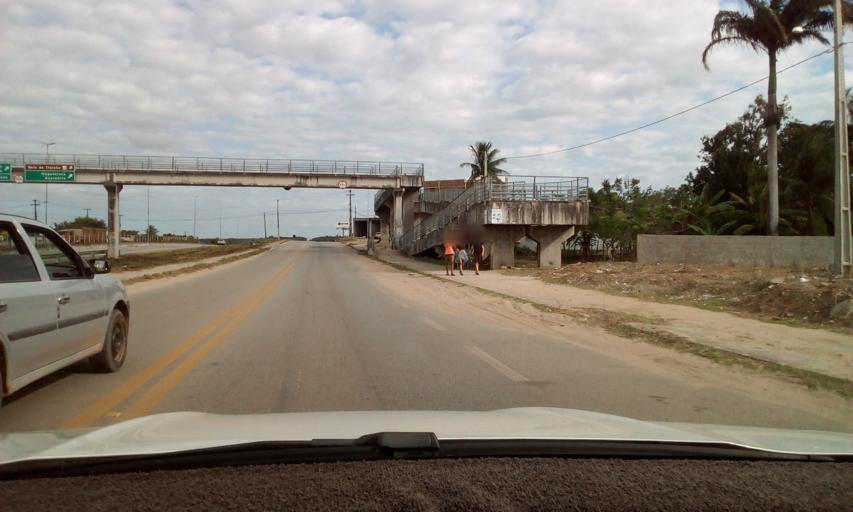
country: BR
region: Paraiba
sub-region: Mamanguape
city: Mamanguape
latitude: -6.8435
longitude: -35.1362
